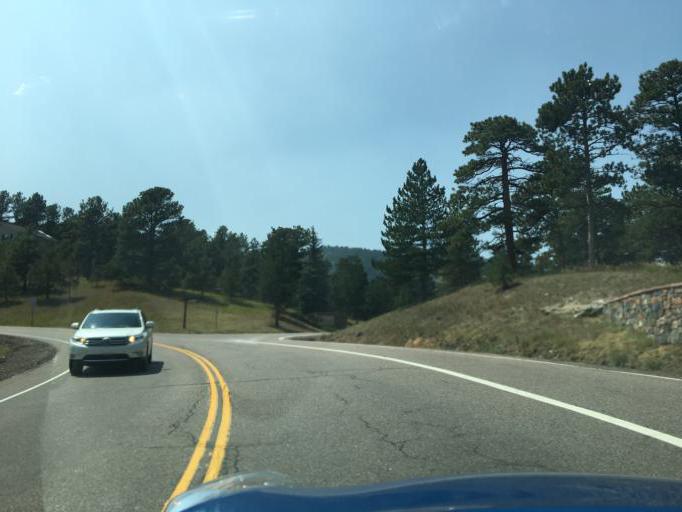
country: US
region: Colorado
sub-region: Jefferson County
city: Genesee
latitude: 39.7023
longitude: -105.2628
